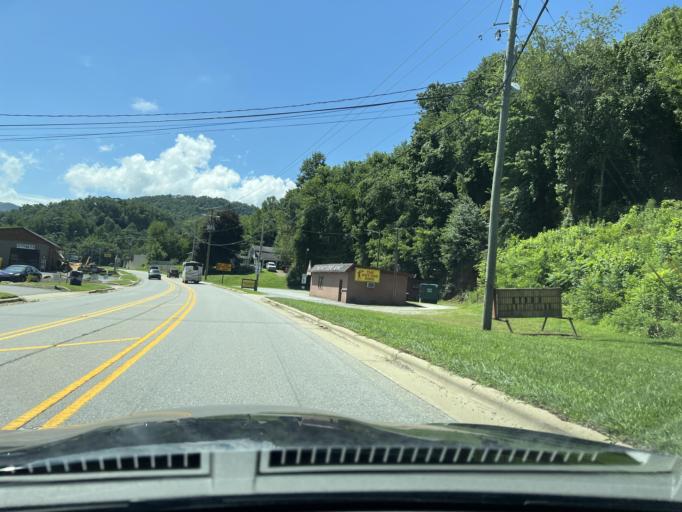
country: US
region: North Carolina
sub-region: Buncombe County
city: Fairview
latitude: 35.5199
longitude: -82.4043
